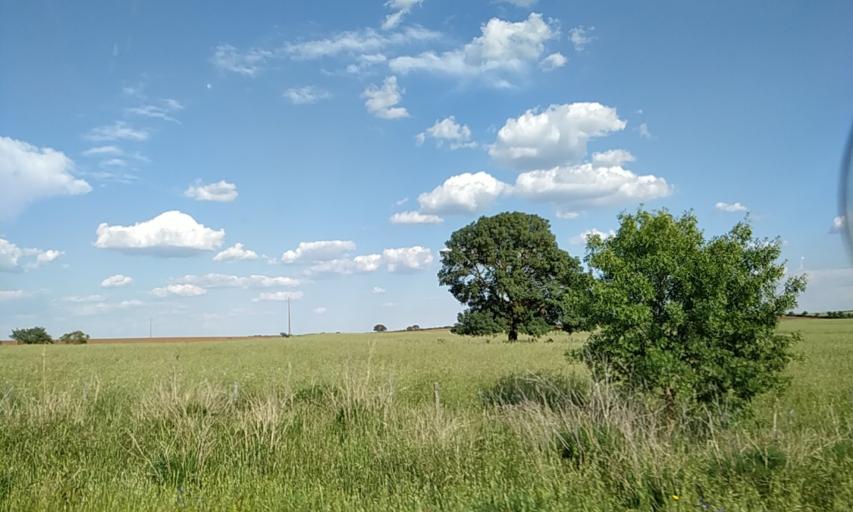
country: PT
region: Evora
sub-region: Estremoz
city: Estremoz
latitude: 38.9684
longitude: -7.4936
